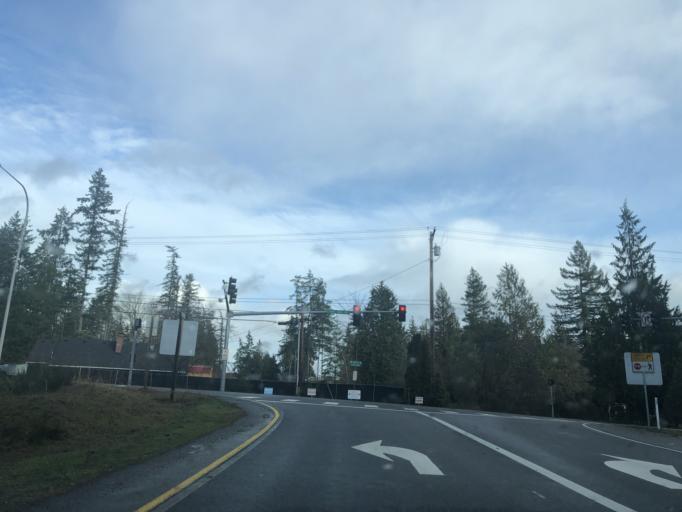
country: US
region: Washington
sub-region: Kitsap County
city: Poulsbo
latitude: 47.7521
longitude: -122.6628
